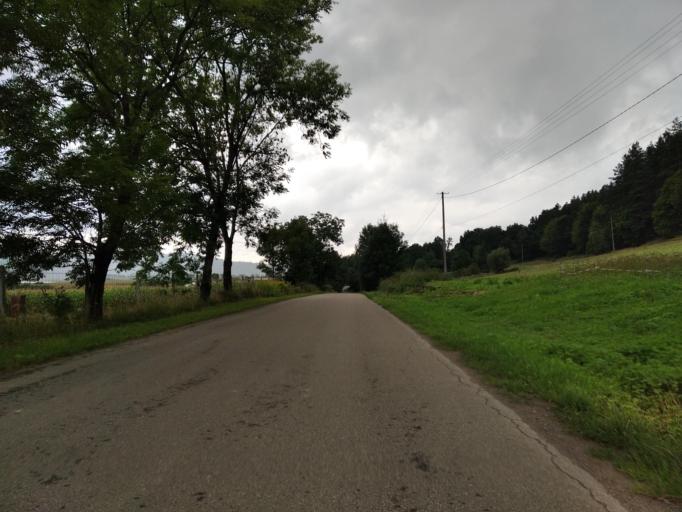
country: PL
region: Subcarpathian Voivodeship
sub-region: Powiat brzozowski
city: Dydnia
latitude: 49.6746
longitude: 22.2756
